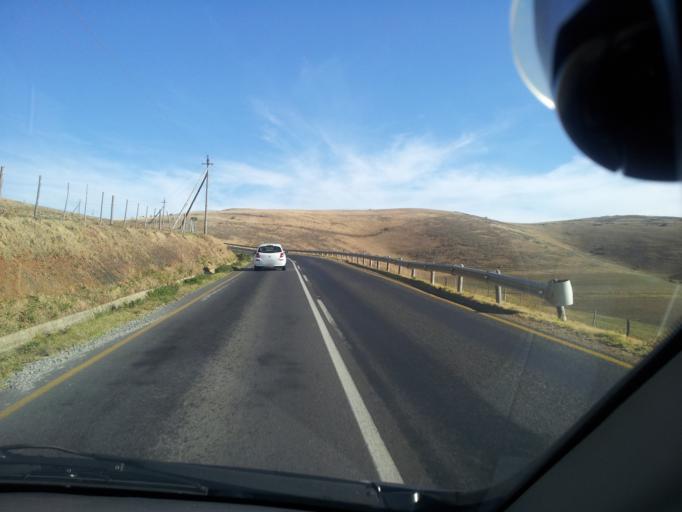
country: ZA
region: Western Cape
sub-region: City of Cape Town
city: Kraaifontein
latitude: -33.7980
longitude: 18.6082
